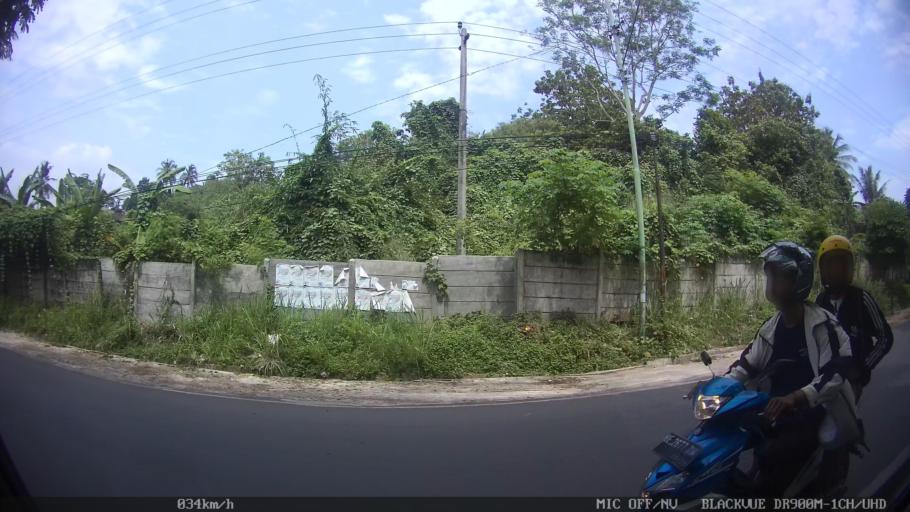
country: ID
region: Lampung
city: Bandarlampung
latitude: -5.4151
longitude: 105.2469
